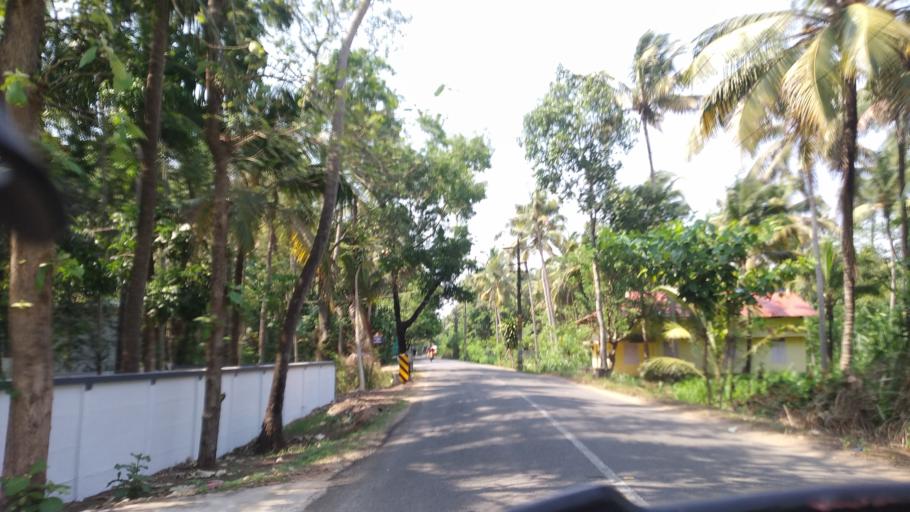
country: IN
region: Kerala
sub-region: Thrissur District
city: Kodungallur
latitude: 10.2716
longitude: 76.1402
